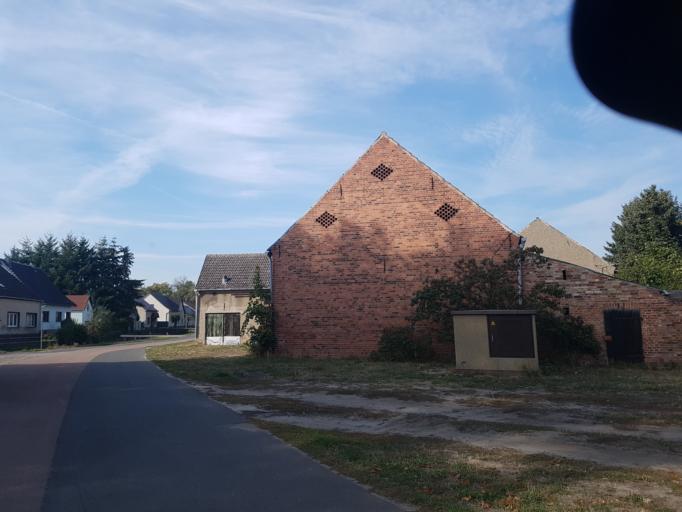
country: DE
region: Brandenburg
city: Ihlow
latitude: 51.8823
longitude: 13.2465
